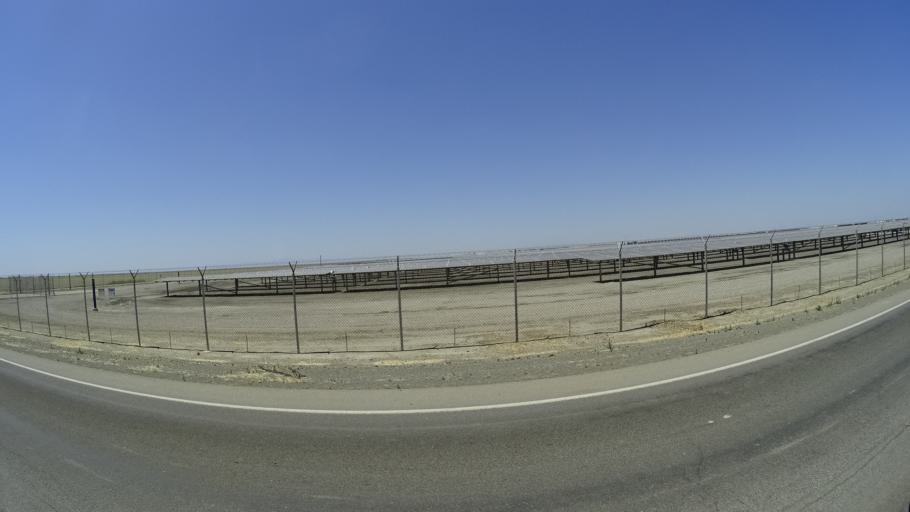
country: US
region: California
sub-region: Kings County
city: Corcoran
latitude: 36.1603
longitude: -119.6458
